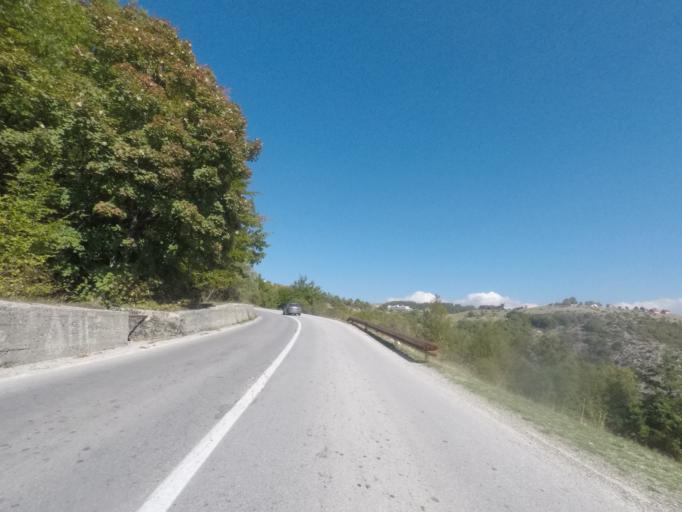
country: ME
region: Opstina Pluzine
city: Pluzine
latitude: 43.1128
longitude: 18.8225
